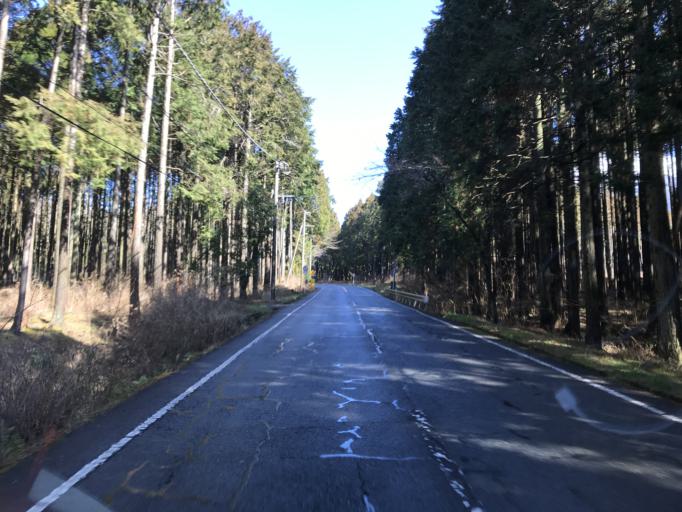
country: JP
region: Shizuoka
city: Fujinomiya
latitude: 35.2873
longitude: 138.6624
